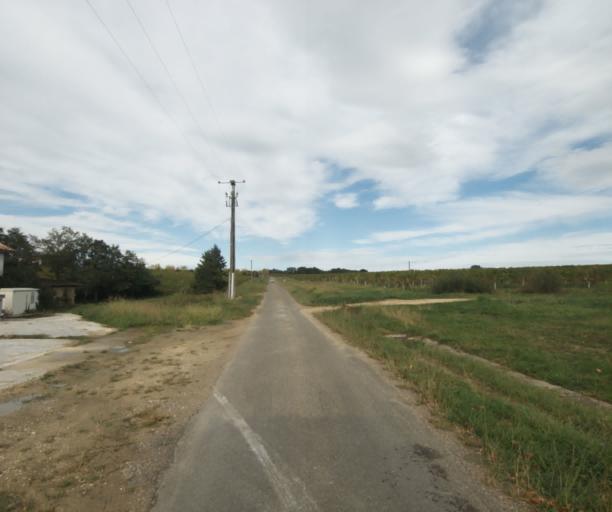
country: FR
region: Midi-Pyrenees
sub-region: Departement du Gers
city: Cazaubon
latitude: 43.8813
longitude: -0.1365
